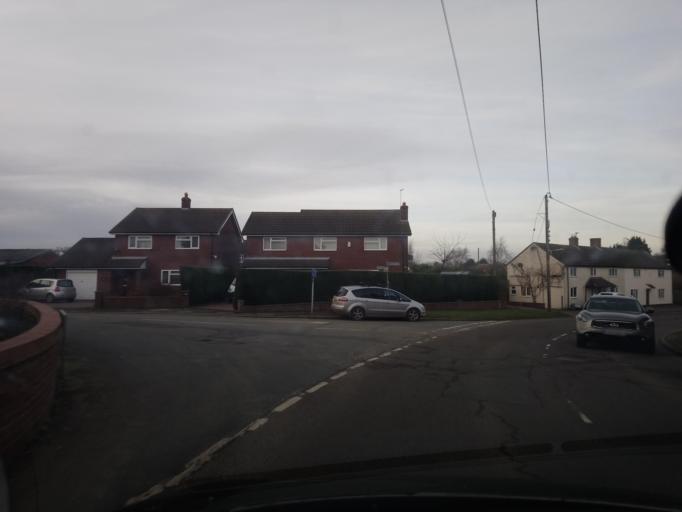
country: GB
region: England
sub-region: Shropshire
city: Whitchurch
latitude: 52.9363
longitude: -2.6840
